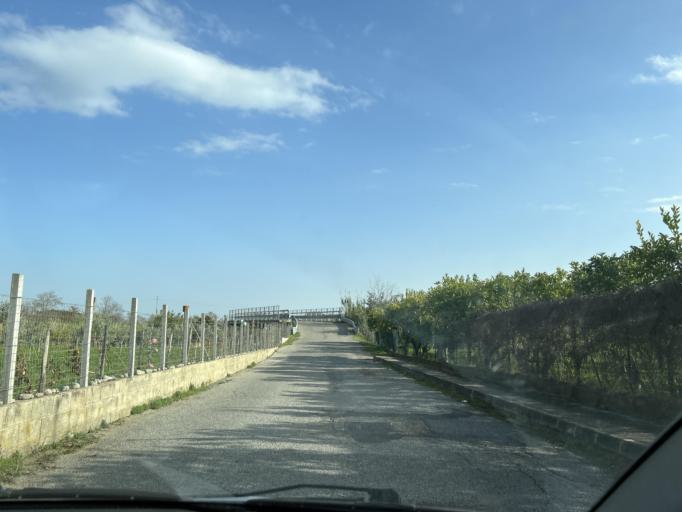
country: IT
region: Calabria
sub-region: Provincia di Catanzaro
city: Montepaone Lido
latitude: 38.7149
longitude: 16.5279
